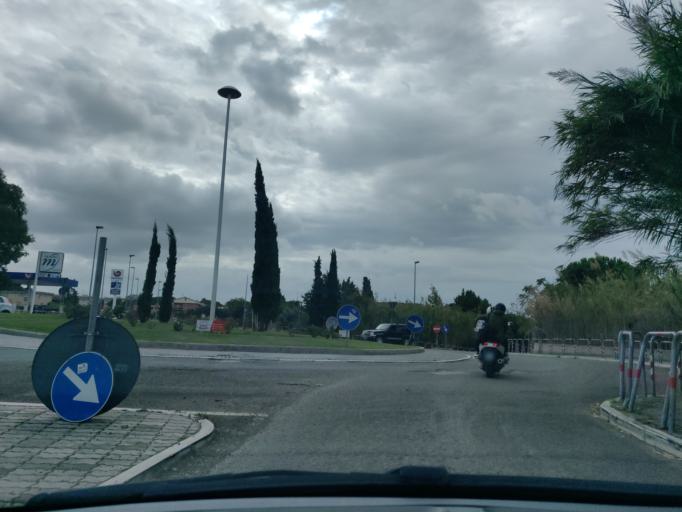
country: IT
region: Latium
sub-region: Citta metropolitana di Roma Capitale
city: Civitavecchia
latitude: 42.1010
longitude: 11.7948
